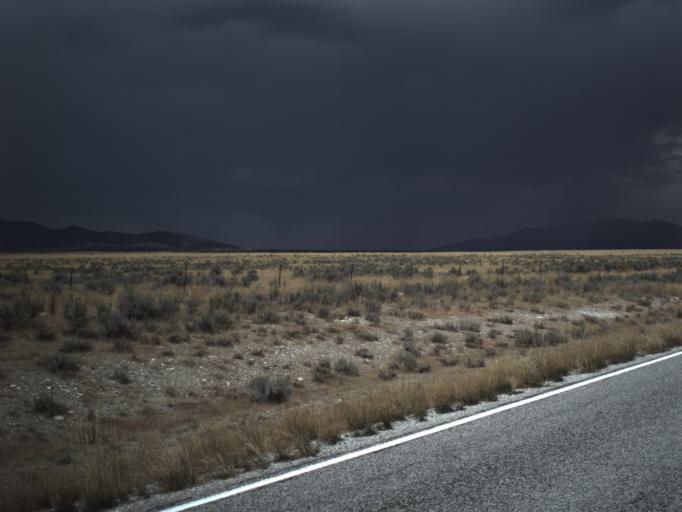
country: US
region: Idaho
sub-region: Minidoka County
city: Rupert
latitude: 41.8591
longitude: -113.1295
